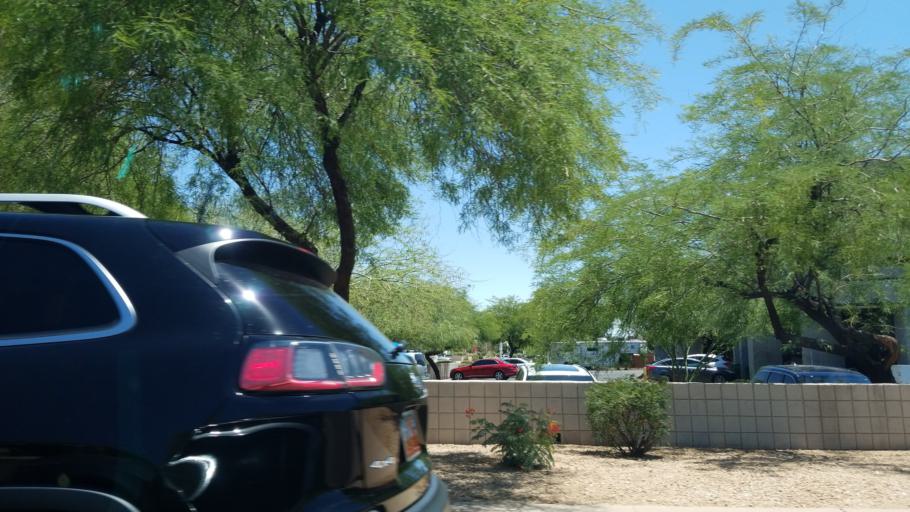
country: US
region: Arizona
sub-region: Maricopa County
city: Paradise Valley
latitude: 33.6249
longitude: -111.9042
